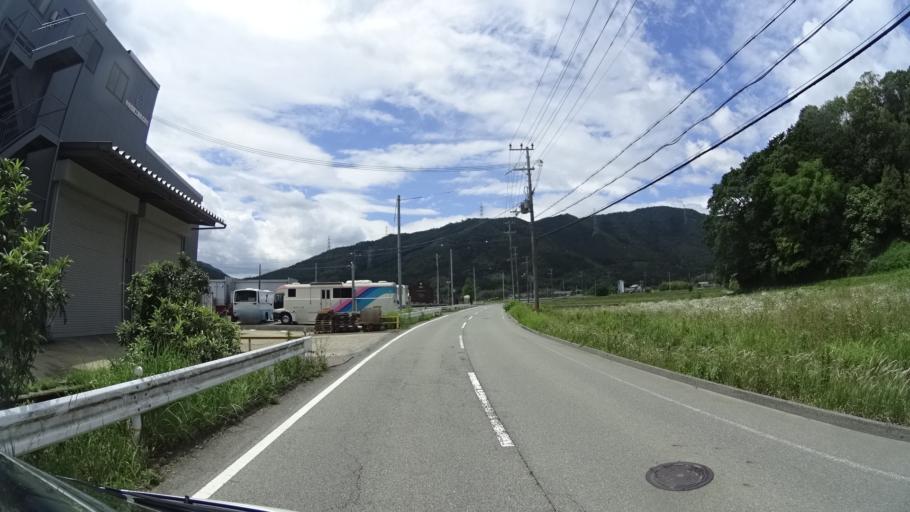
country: JP
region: Kyoto
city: Kameoka
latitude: 35.0071
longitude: 135.4804
